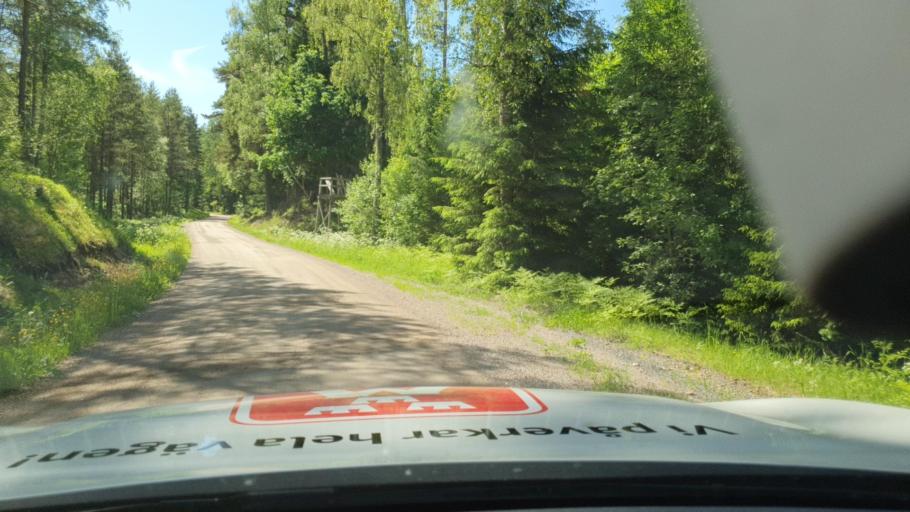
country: SE
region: Joenkoeping
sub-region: Mullsjo Kommun
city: Mullsjoe
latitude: 58.0403
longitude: 13.8553
